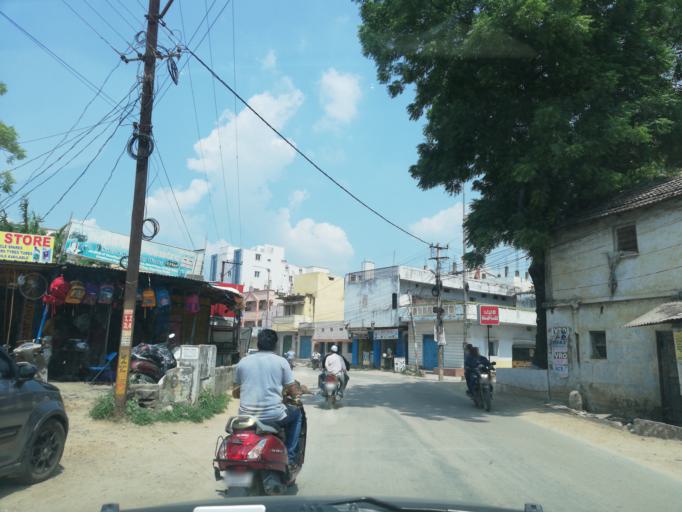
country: IN
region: Telangana
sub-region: Medak
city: Serilingampalle
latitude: 17.4897
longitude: 78.3193
